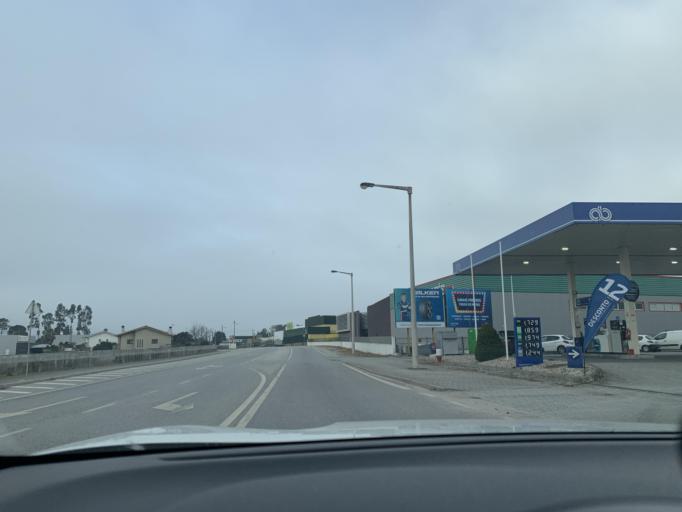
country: PT
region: Viseu
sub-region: Viseu
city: Rio de Loba
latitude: 40.6280
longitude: -7.8825
